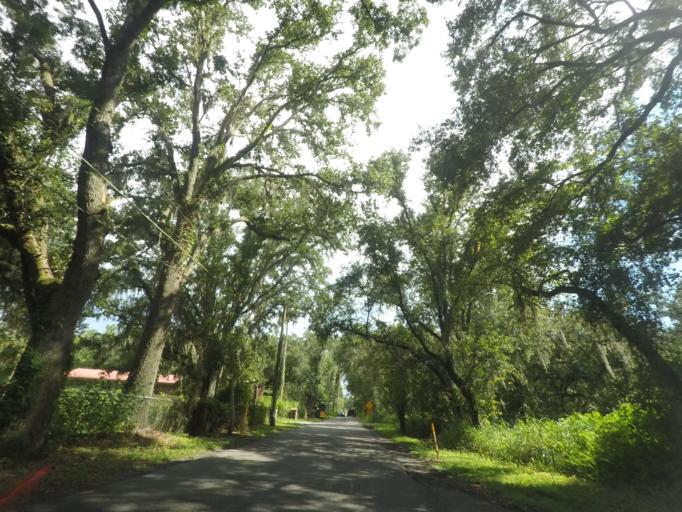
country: US
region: Florida
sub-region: Osceola County
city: Kissimmee
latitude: 28.3202
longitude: -81.4626
